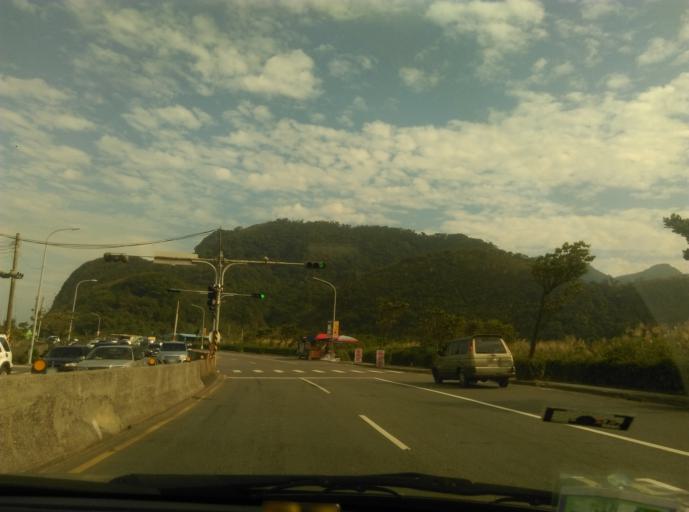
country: TW
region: Taiwan
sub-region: Keelung
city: Keelung
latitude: 25.1794
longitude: 121.6946
